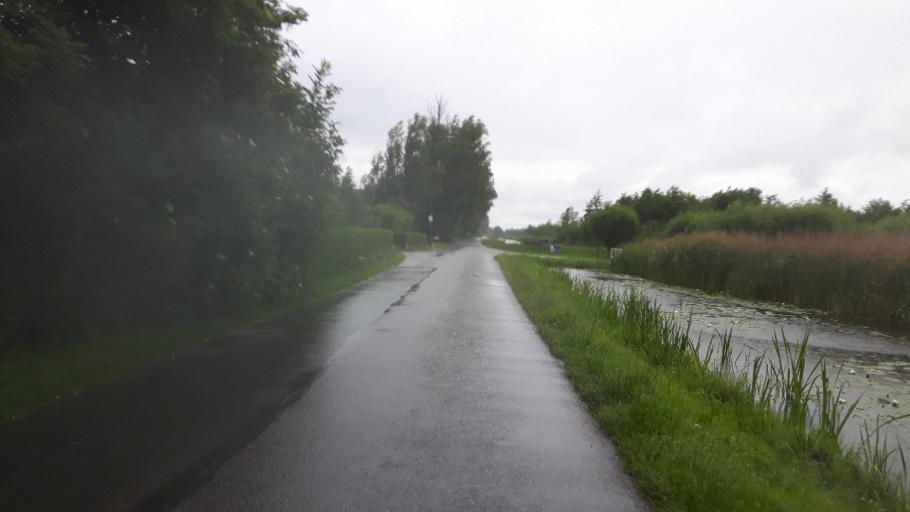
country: NL
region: Utrecht
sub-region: Stichtse Vecht
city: Breukelen
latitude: 52.1378
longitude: 4.9572
